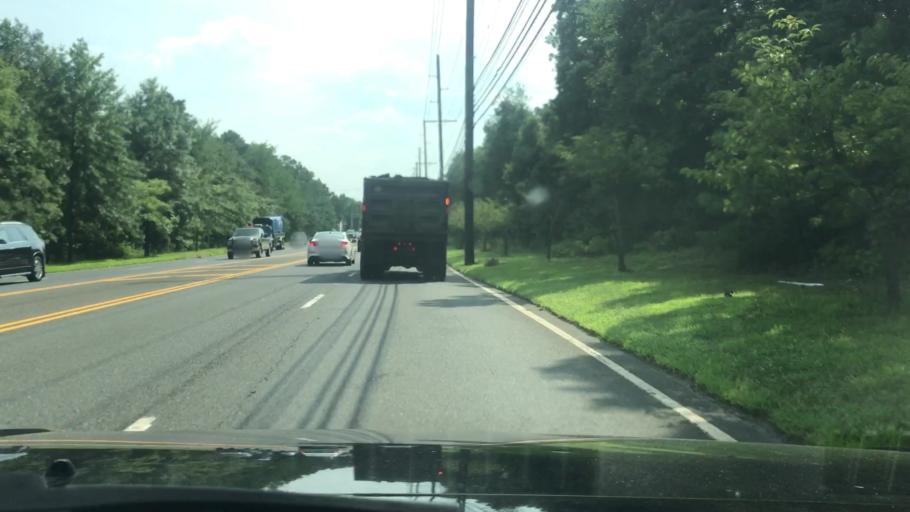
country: US
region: New Jersey
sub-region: Monmouth County
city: Tinton Falls
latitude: 40.2494
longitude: -74.0987
